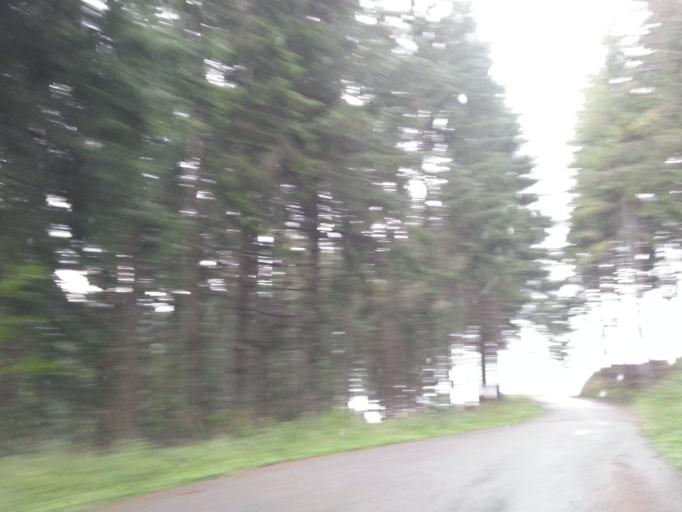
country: FR
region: Rhone-Alpes
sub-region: Departement de la Savoie
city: Marthod
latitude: 45.7037
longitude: 6.4529
